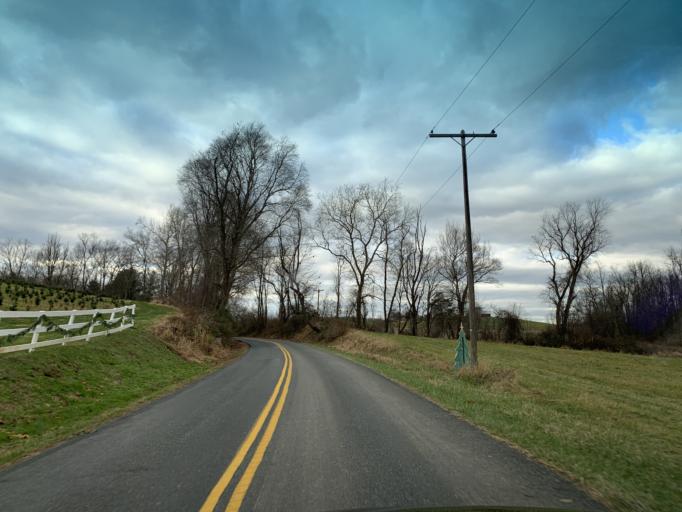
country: US
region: Maryland
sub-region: Harford County
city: Jarrettsville
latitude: 39.6578
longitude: -76.4406
